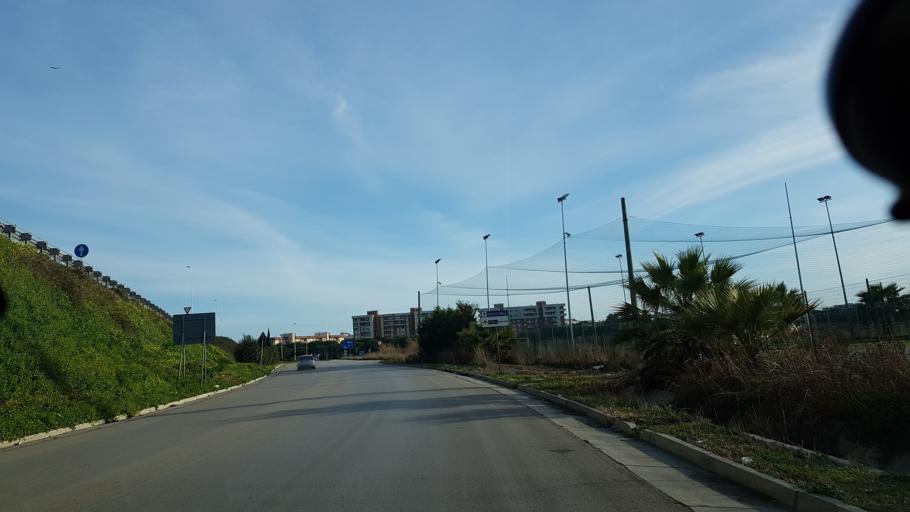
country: IT
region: Apulia
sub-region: Provincia di Brindisi
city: Brindisi
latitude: 40.6252
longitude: 17.9202
